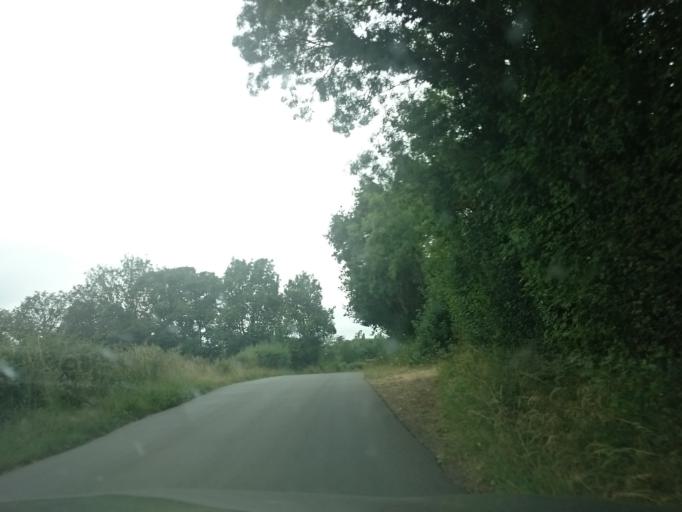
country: FR
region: Pays de la Loire
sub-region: Departement de la Loire-Atlantique
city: Le Pellerin
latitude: 47.2046
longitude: -1.7845
